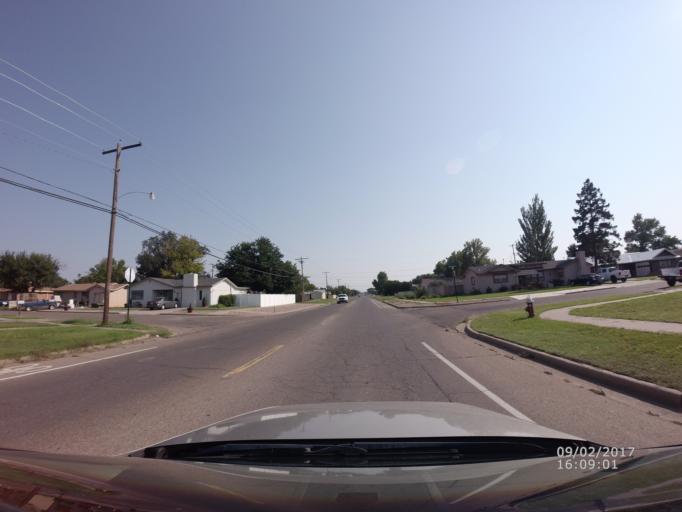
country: US
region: New Mexico
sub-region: Curry County
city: Clovis
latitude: 34.4248
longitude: -103.2142
